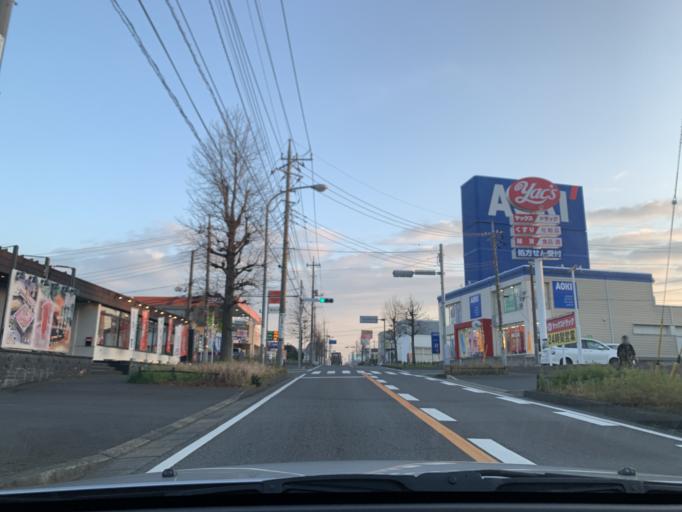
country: JP
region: Chiba
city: Matsudo
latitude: 35.7678
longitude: 139.9107
